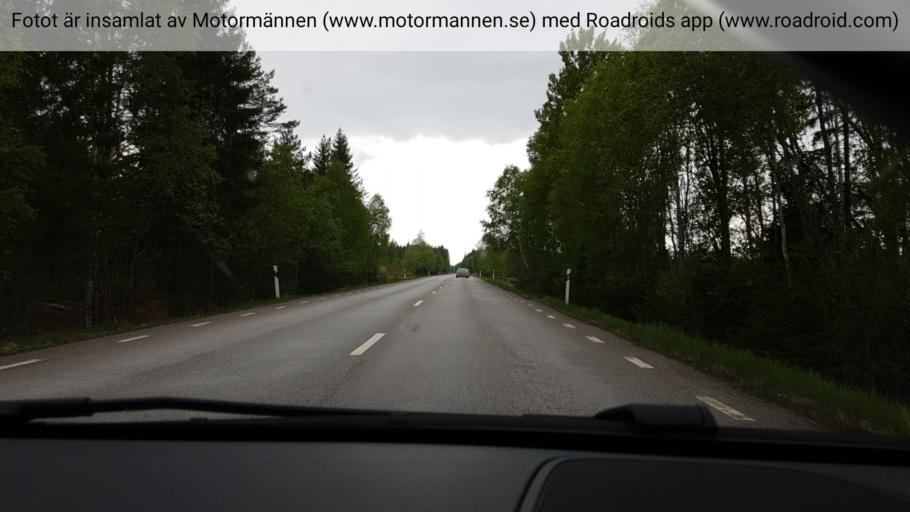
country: SE
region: Uppsala
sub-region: Osthammars Kommun
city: Gimo
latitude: 60.1650
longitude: 18.1483
